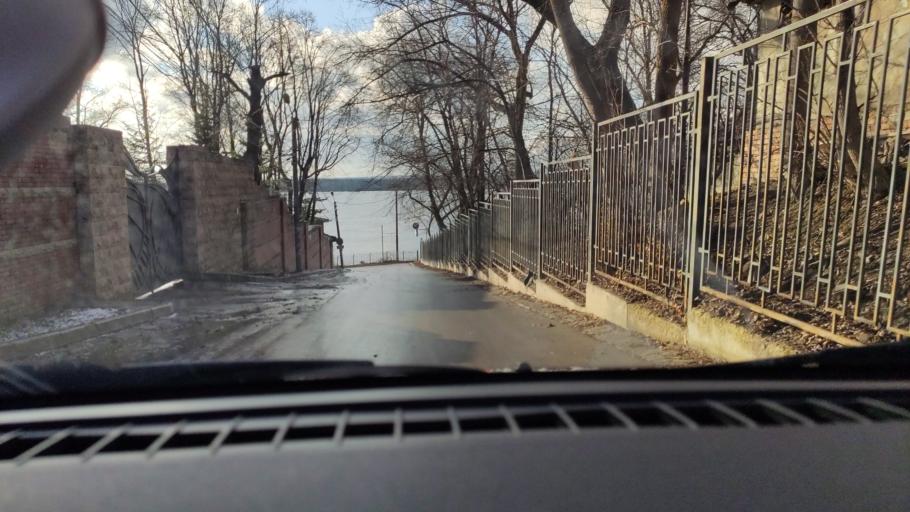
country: RU
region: Samara
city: Samara
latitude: 53.2633
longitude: 50.1840
